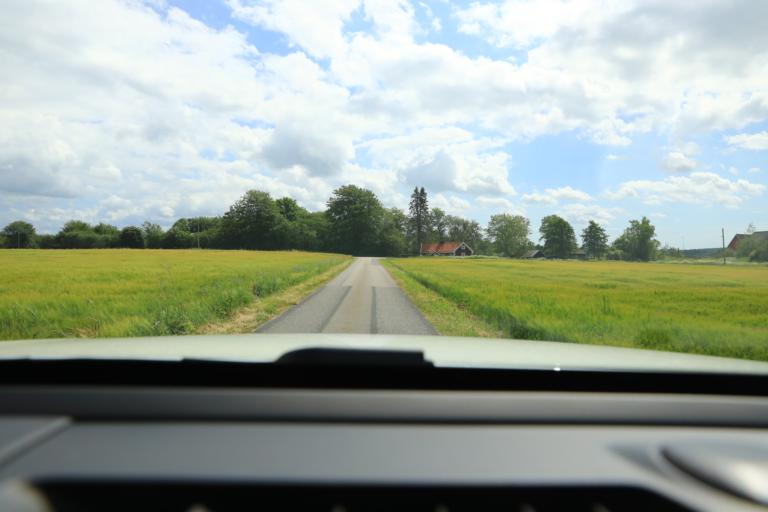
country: SE
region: Halland
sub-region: Varbergs Kommun
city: Tvaaker
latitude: 57.0833
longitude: 12.3975
